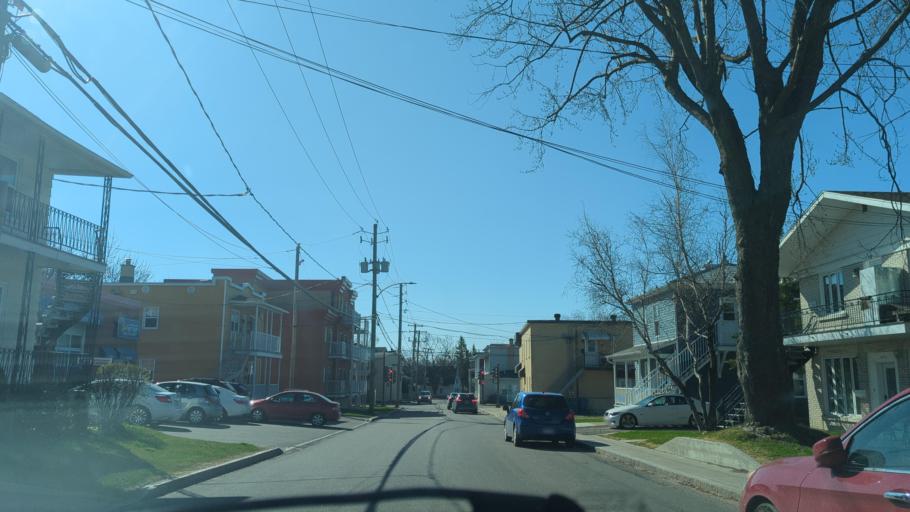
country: CA
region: Quebec
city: Quebec
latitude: 46.8523
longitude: -71.2122
